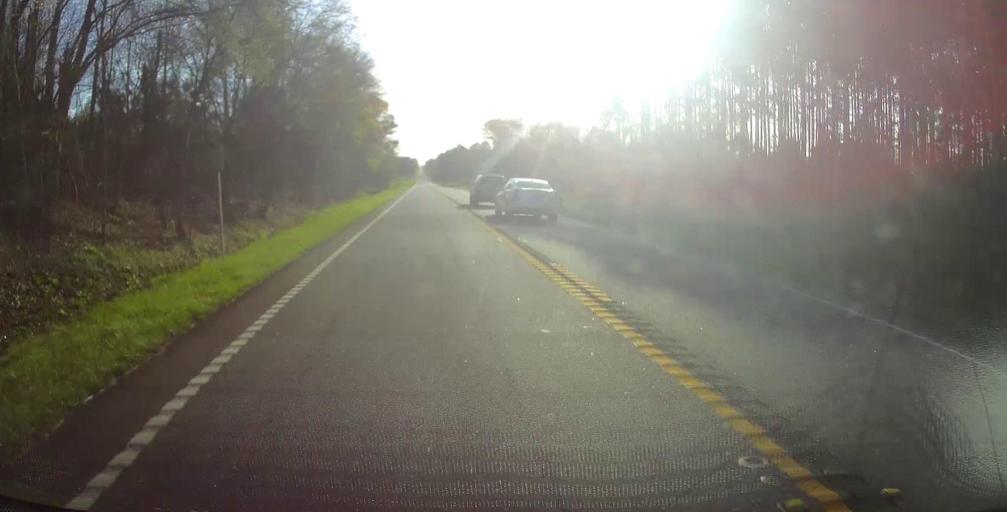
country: US
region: Georgia
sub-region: Tattnall County
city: Reidsville
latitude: 32.1334
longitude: -82.0457
